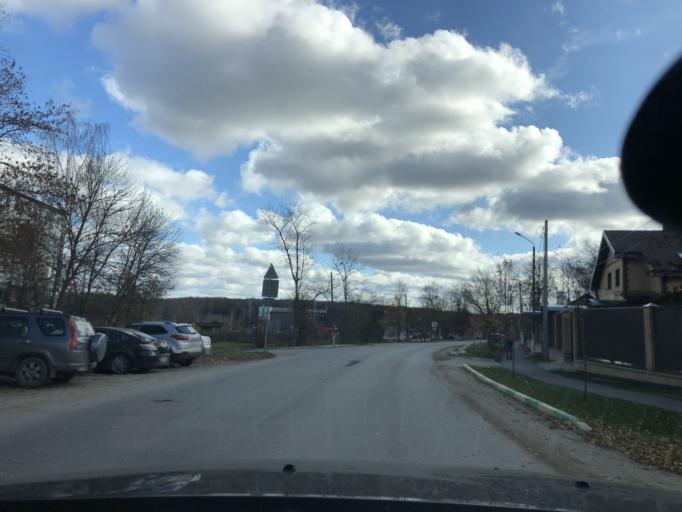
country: RU
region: Tula
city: Gorelki
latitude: 54.2953
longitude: 37.5756
